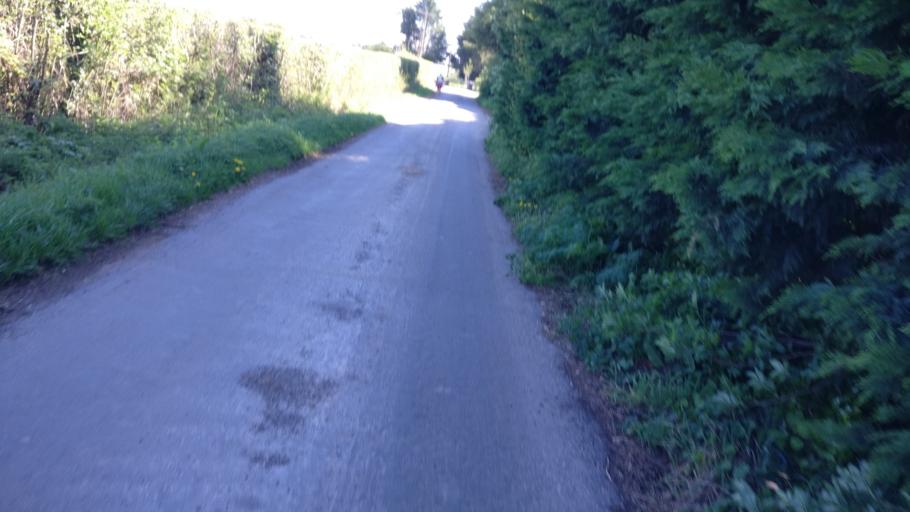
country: GB
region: England
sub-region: Hampshire
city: Basingstoke
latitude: 51.2367
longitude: -1.0867
